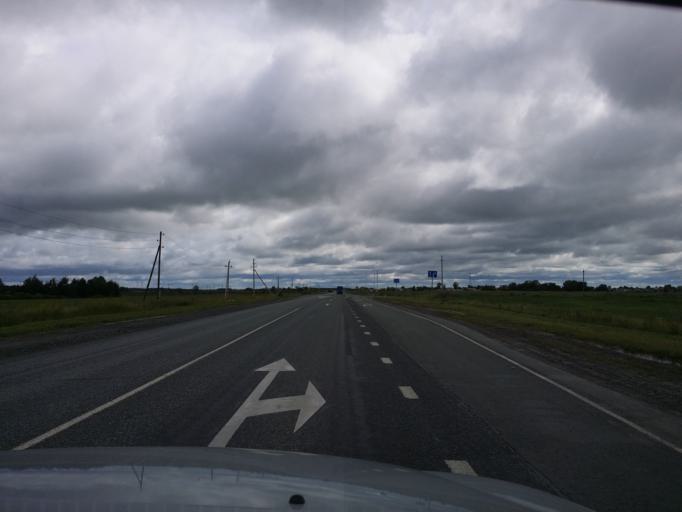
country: RU
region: Tjumen
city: Yarkovo
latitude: 57.2407
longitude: 66.7556
